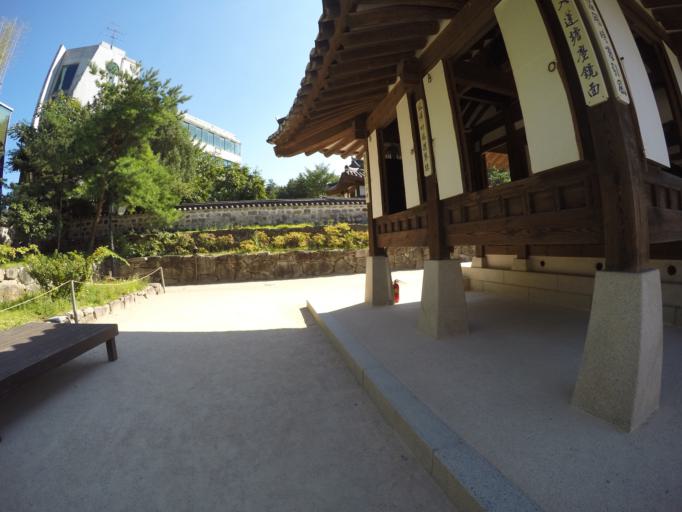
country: KR
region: Seoul
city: Seoul
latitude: 37.5590
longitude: 126.9950
